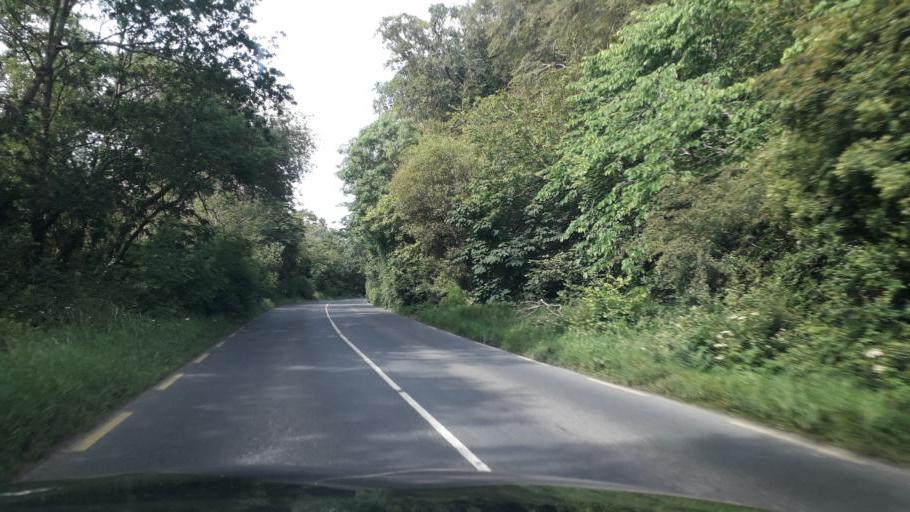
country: IE
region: Leinster
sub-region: Loch Garman
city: Castlebridge
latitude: 52.4076
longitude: -6.4255
